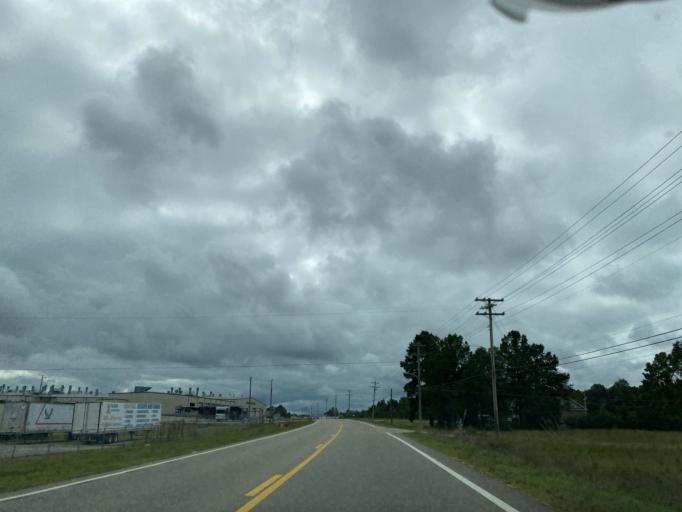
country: US
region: Mississippi
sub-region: Tishomingo County
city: Belmont
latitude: 34.4864
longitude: -88.2069
